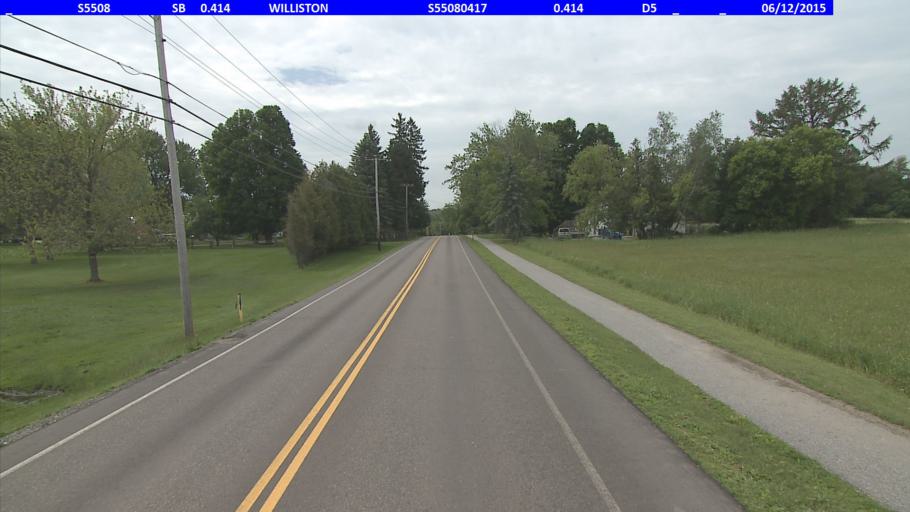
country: US
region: Vermont
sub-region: Chittenden County
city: Williston
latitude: 44.4427
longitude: -73.0645
